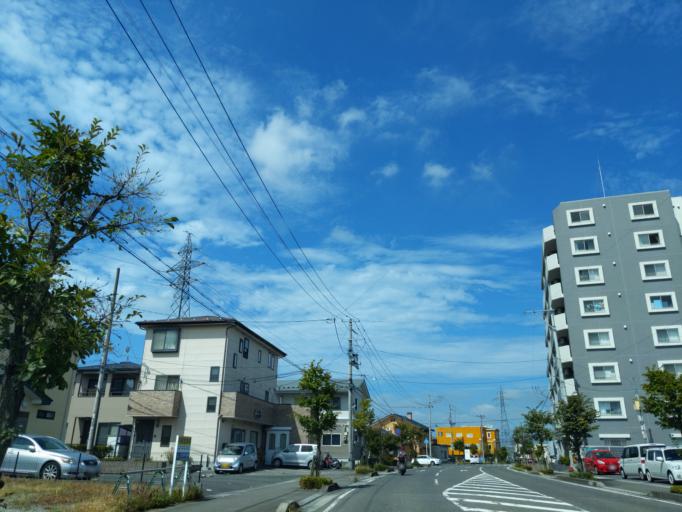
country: JP
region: Fukushima
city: Koriyama
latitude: 37.4221
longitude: 140.3733
